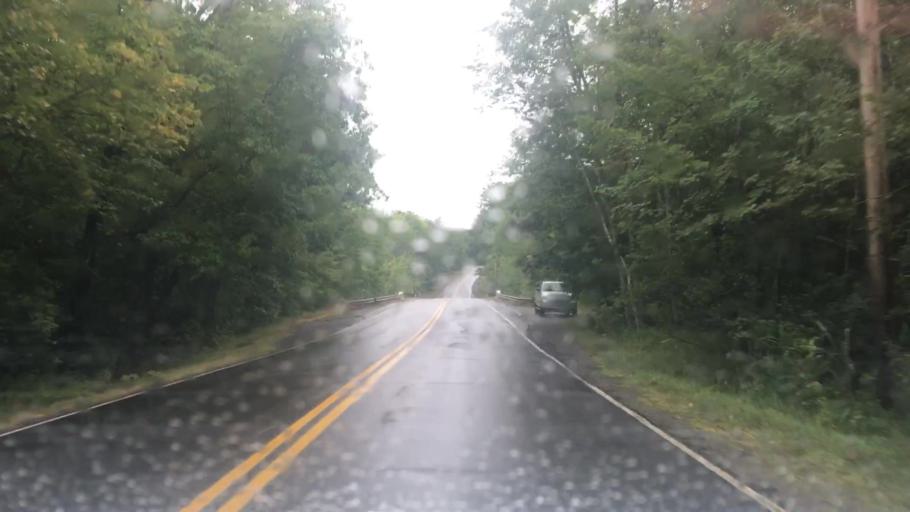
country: US
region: Maine
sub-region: Penobscot County
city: Hudson
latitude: 44.9858
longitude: -68.7942
